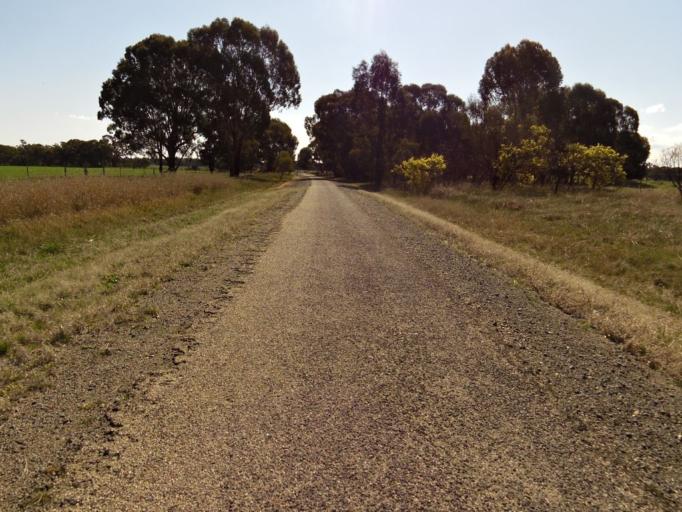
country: AU
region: New South Wales
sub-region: Corowa Shire
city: Corowa
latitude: -36.0380
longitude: 146.4523
